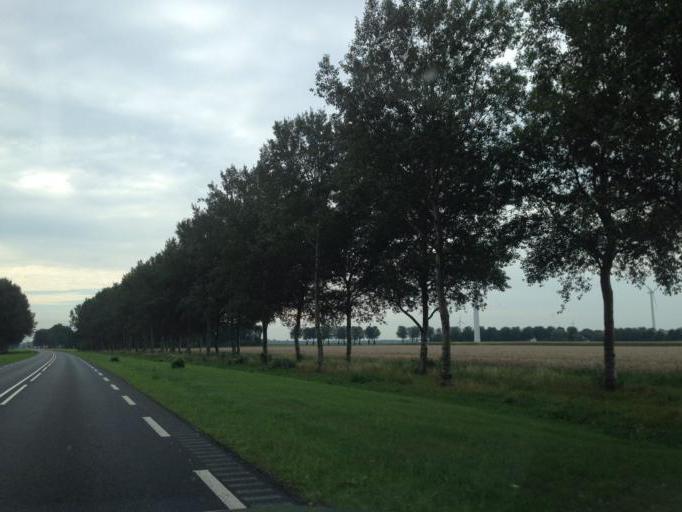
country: NL
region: Utrecht
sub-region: Gemeente Bunschoten
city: Spakenburg
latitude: 52.3614
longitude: 5.3642
